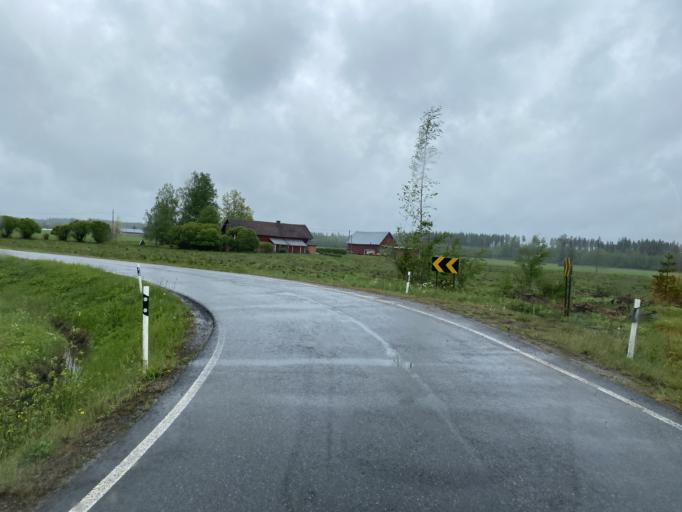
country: FI
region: Haeme
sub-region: Forssa
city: Humppila
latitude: 61.0554
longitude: 23.3262
